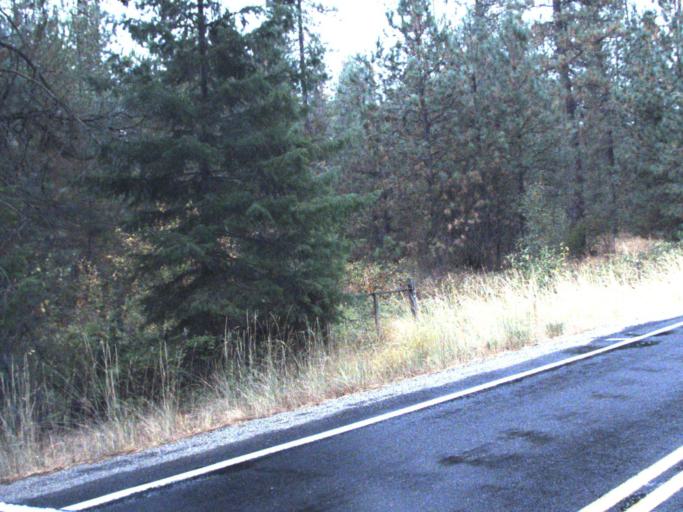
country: US
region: Washington
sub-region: Stevens County
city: Chewelah
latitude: 48.0333
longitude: -117.7335
